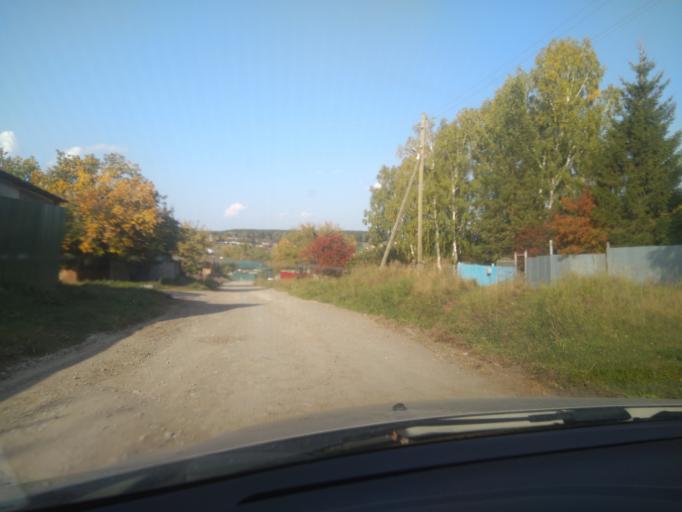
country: RU
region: Sverdlovsk
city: Pokrovskoye
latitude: 56.4317
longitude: 61.5933
